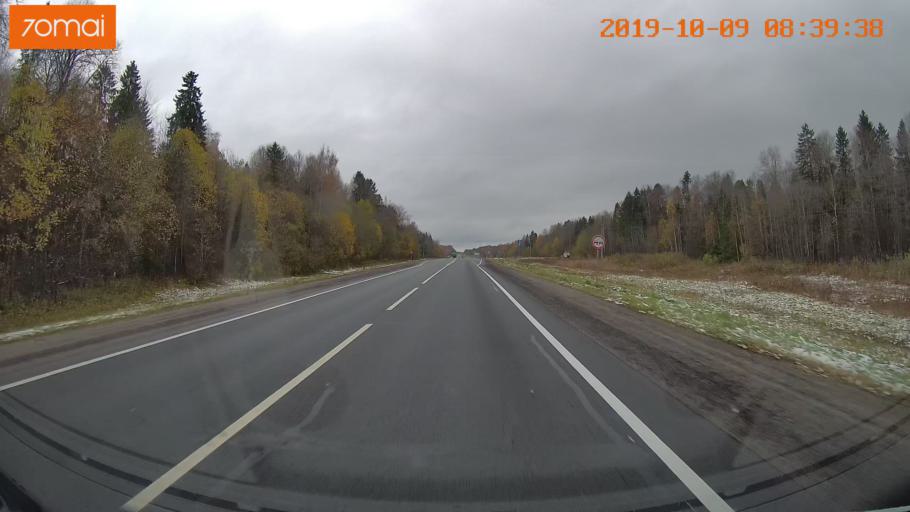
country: RU
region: Vologda
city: Gryazovets
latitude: 58.9746
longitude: 40.1506
